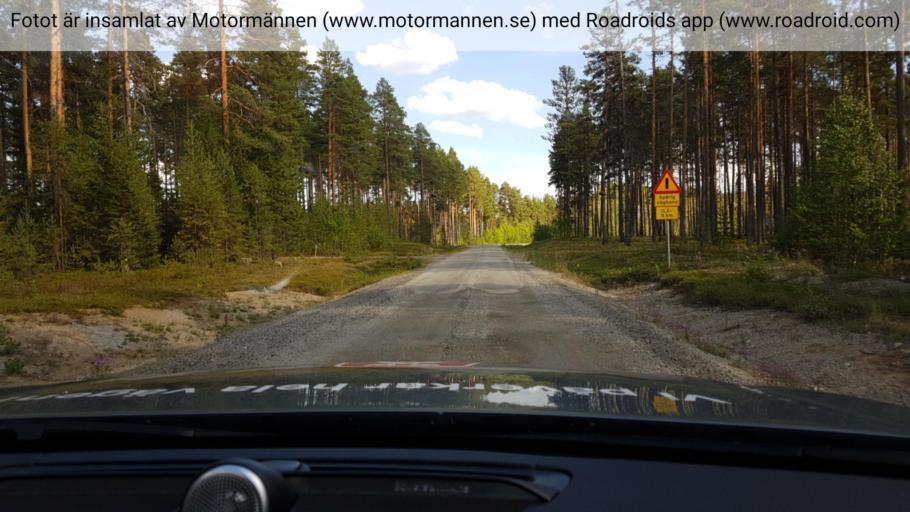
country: SE
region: Vaesterbotten
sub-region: Dorotea Kommun
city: Dorotea
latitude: 63.9204
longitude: 16.2597
